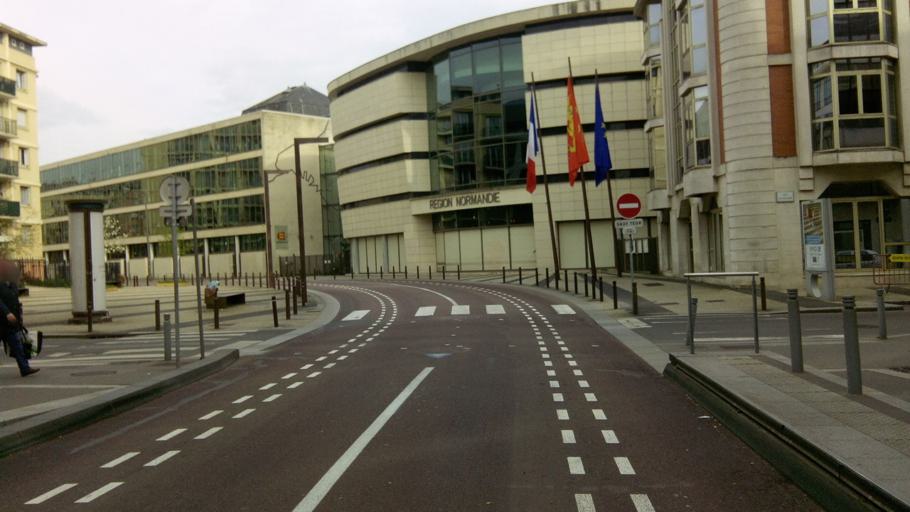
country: FR
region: Haute-Normandie
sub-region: Departement de la Seine-Maritime
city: Rouen
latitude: 49.4380
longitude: 1.1018
